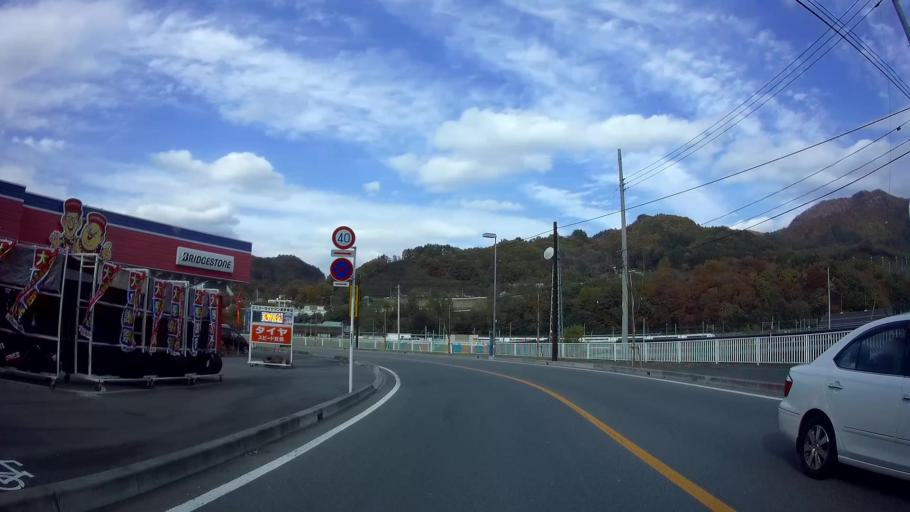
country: JP
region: Gunma
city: Nakanojomachi
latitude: 36.5434
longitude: 138.6492
